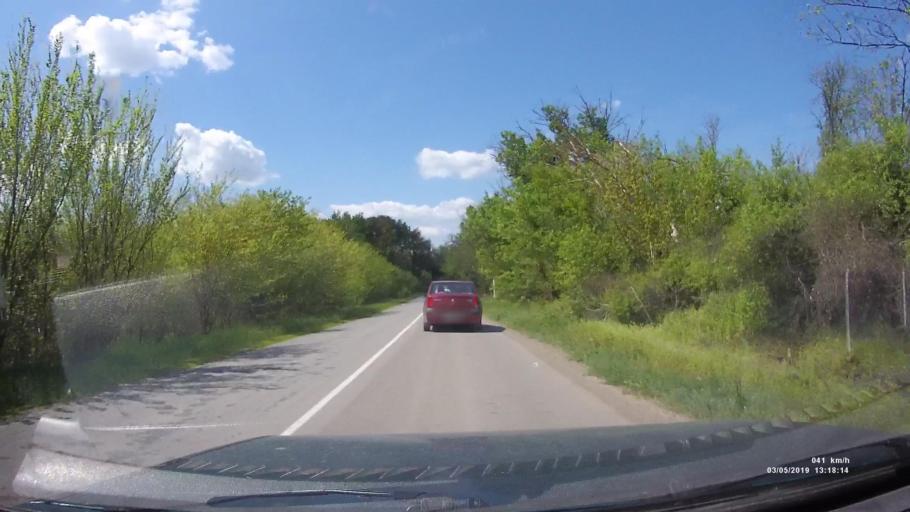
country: RU
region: Rostov
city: Semikarakorsk
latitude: 47.5317
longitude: 40.7495
